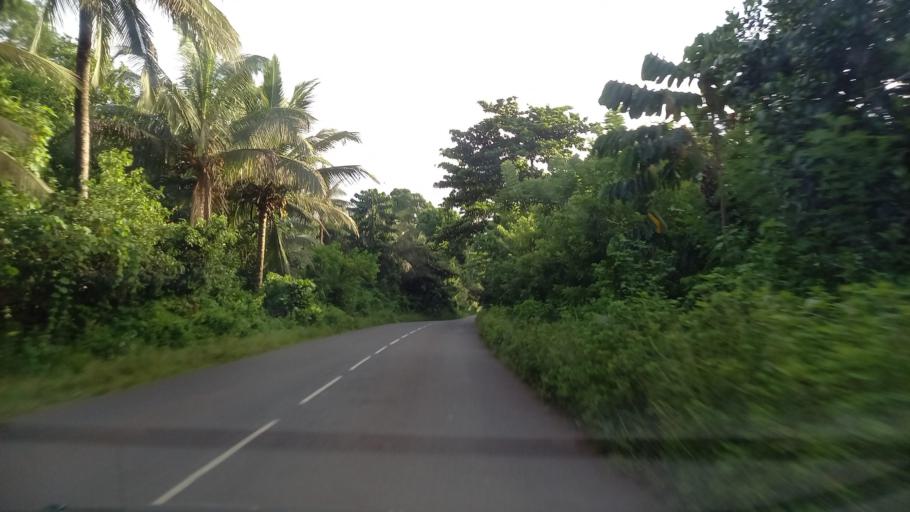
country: YT
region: Bandraboua
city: Bandraboua
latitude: -12.7316
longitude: 45.1196
